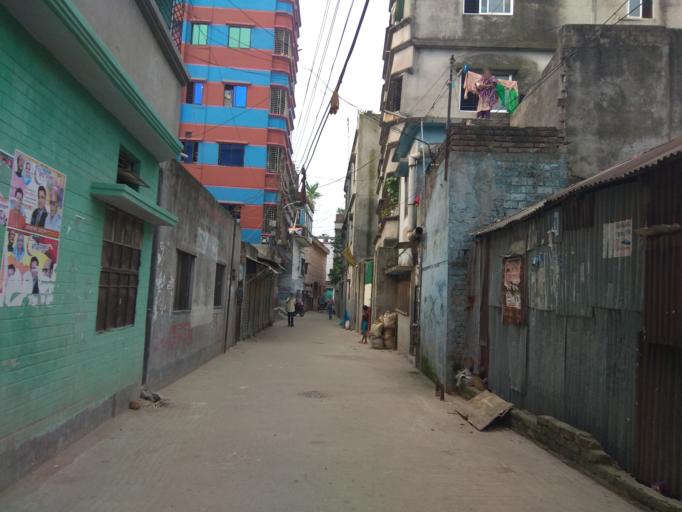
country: BD
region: Dhaka
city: Azimpur
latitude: 23.7189
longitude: 90.3739
